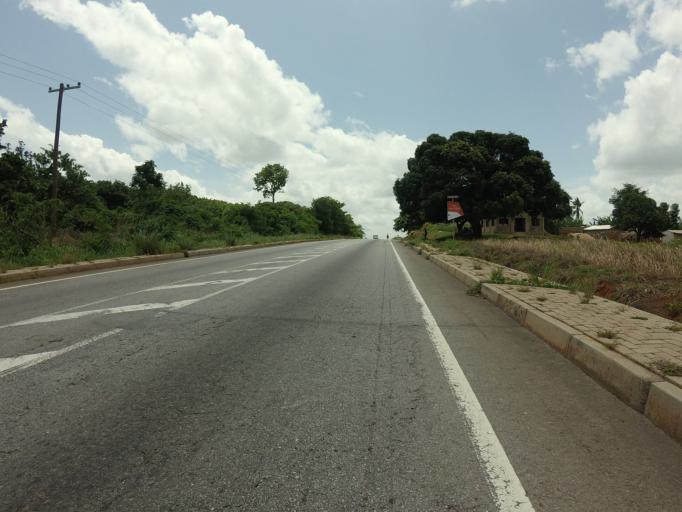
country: GH
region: Brong-Ahafo
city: Techiman
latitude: 7.7205
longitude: -1.8405
